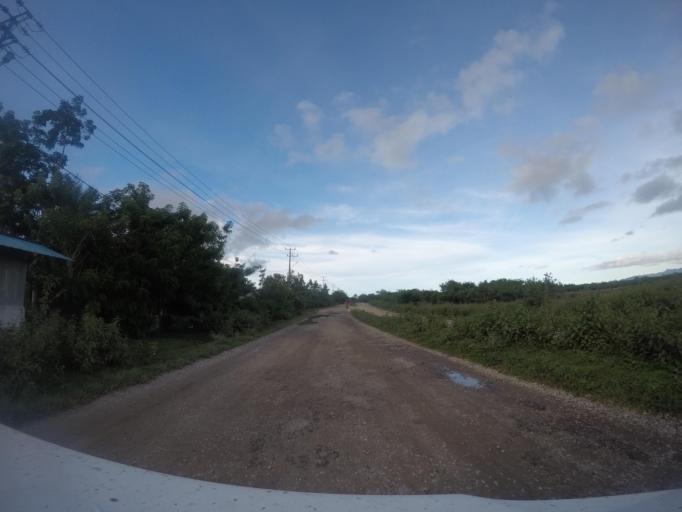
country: TL
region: Lautem
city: Lospalos
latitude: -8.5088
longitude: 127.0050
